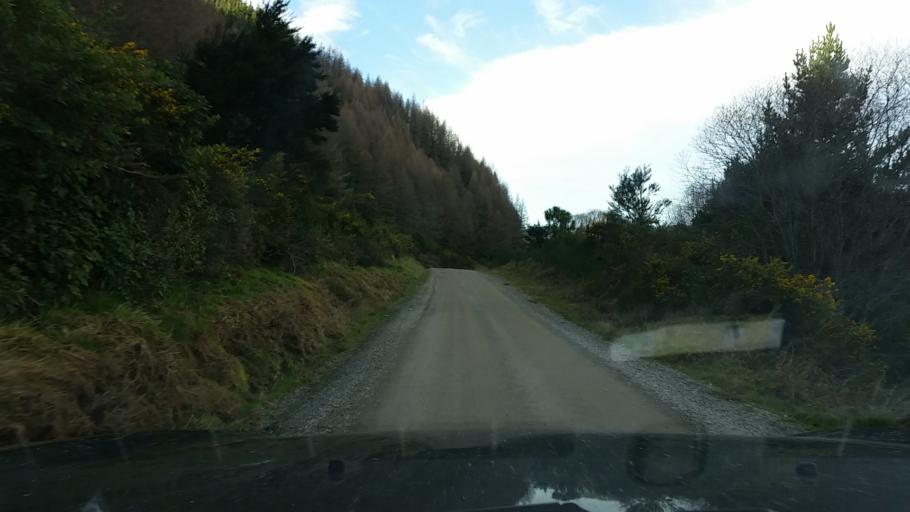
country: NZ
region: Nelson
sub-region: Nelson City
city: Nelson
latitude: -41.5775
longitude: 173.4333
